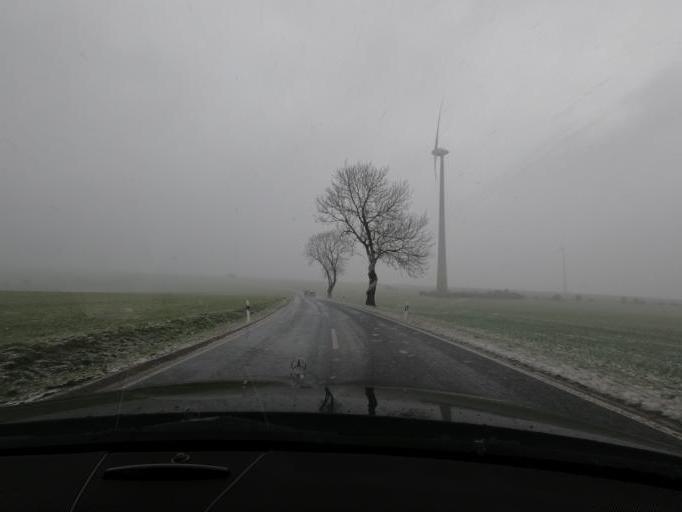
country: DE
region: Thuringia
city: Buttstedt
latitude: 51.2573
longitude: 10.2770
